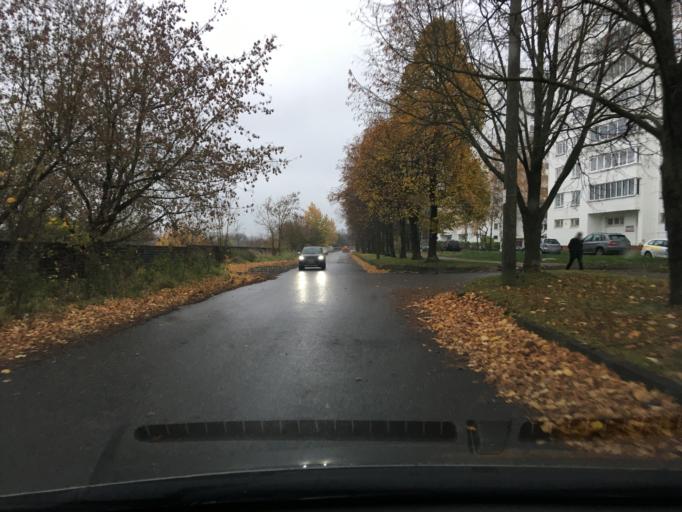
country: EE
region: Harju
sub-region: Tallinna linn
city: Tallinn
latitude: 59.4326
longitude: 24.7890
